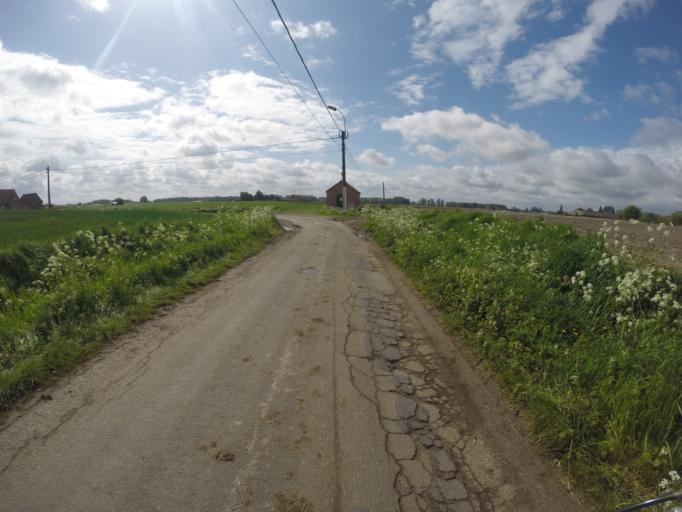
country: BE
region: Flanders
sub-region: Provincie Oost-Vlaanderen
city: Aalter
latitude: 51.0587
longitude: 3.4410
